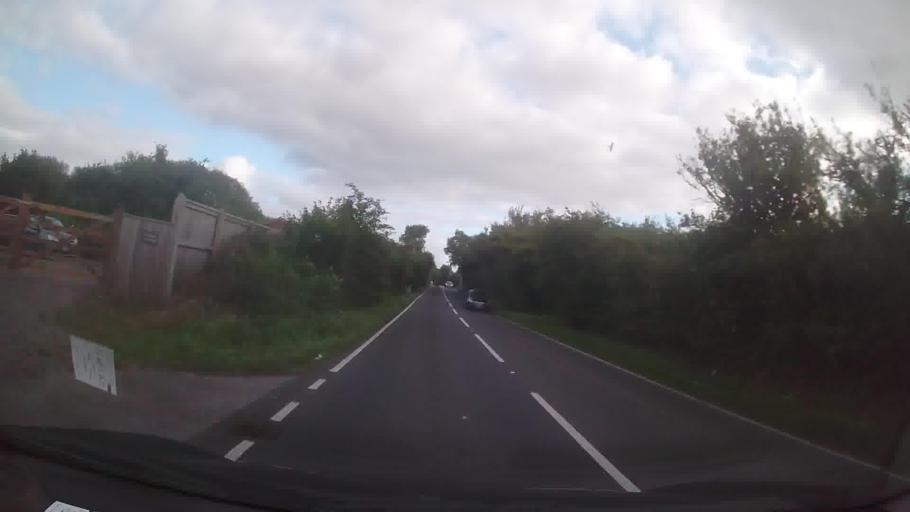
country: GB
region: Wales
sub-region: Pembrokeshire
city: Kilgetty
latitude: 51.7084
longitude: -4.7268
